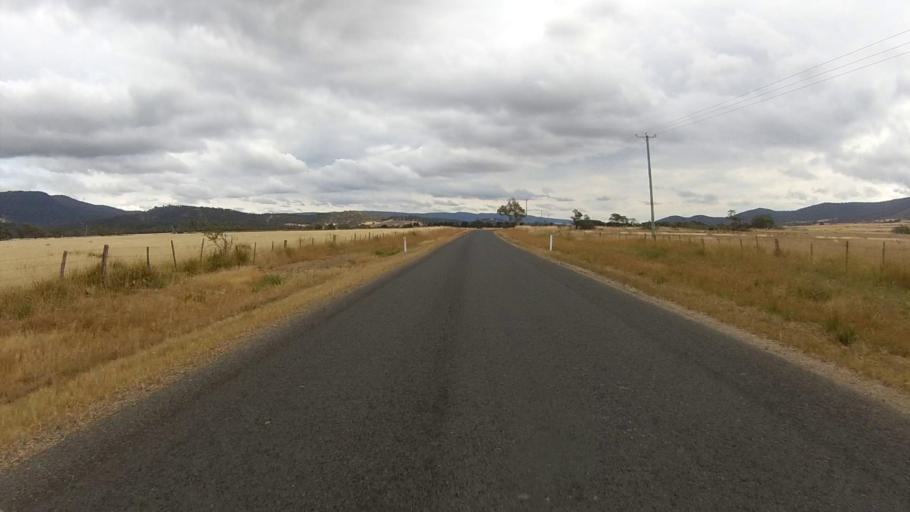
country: AU
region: Tasmania
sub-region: Break O'Day
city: St Helens
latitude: -41.8240
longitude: 147.8611
